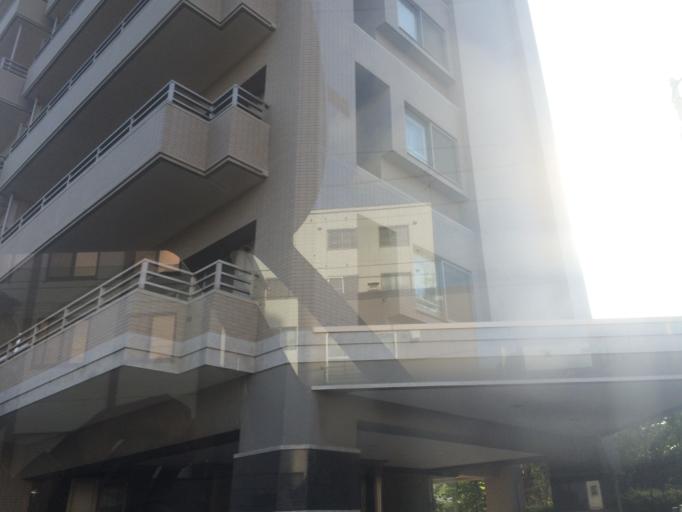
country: JP
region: Hokkaido
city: Sapporo
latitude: 43.0432
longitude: 141.3504
